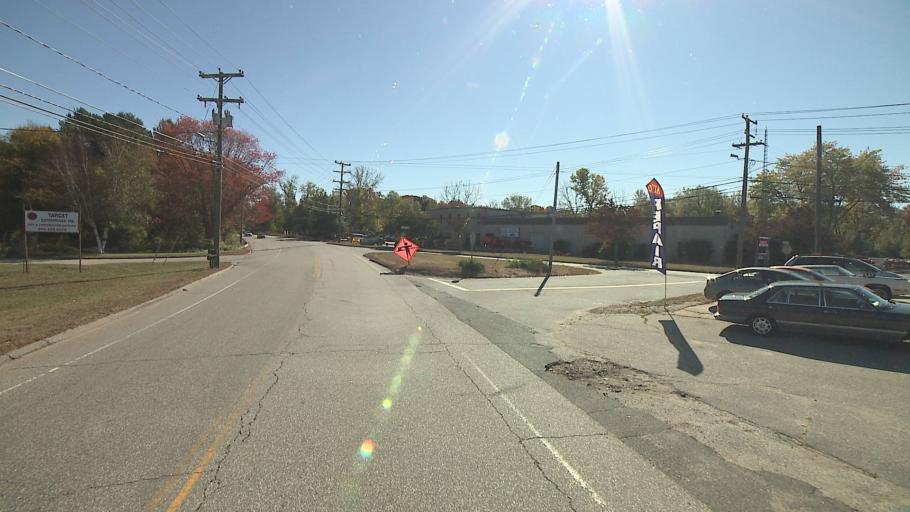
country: US
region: Connecticut
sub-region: Windham County
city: Willimantic
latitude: 41.7177
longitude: -72.2470
